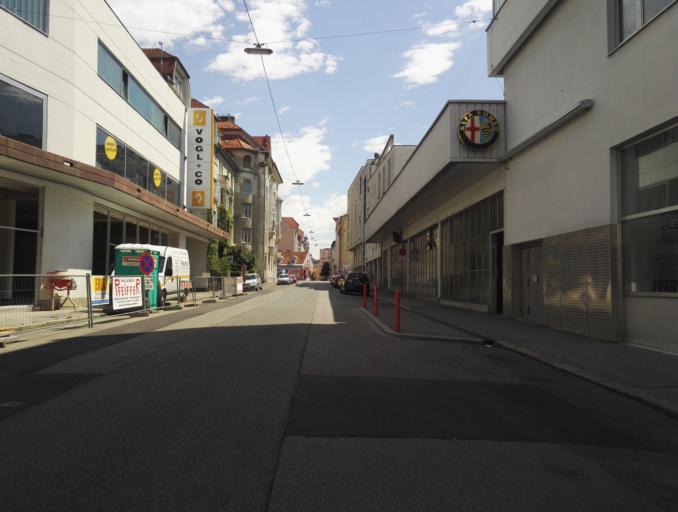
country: AT
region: Styria
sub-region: Graz Stadt
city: Graz
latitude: 47.0630
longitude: 15.4385
